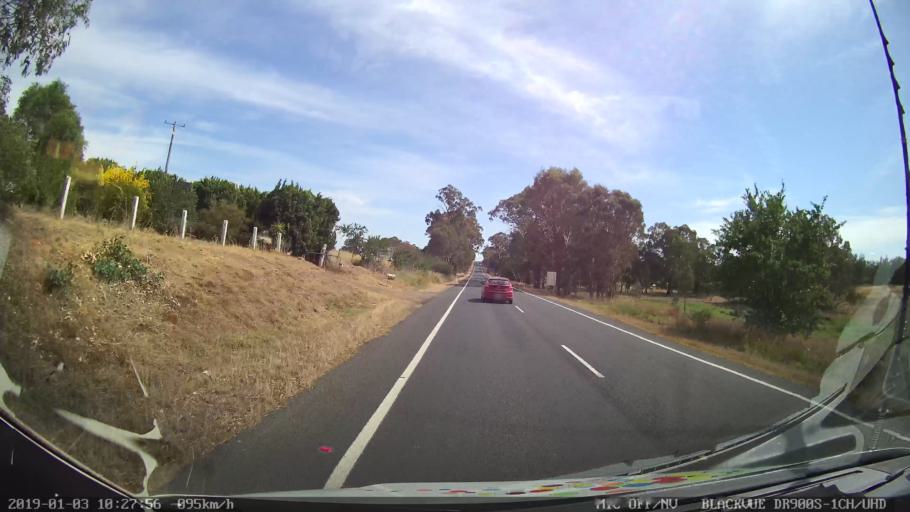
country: AU
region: New South Wales
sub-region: Young
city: Young
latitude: -34.3950
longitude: 148.2586
